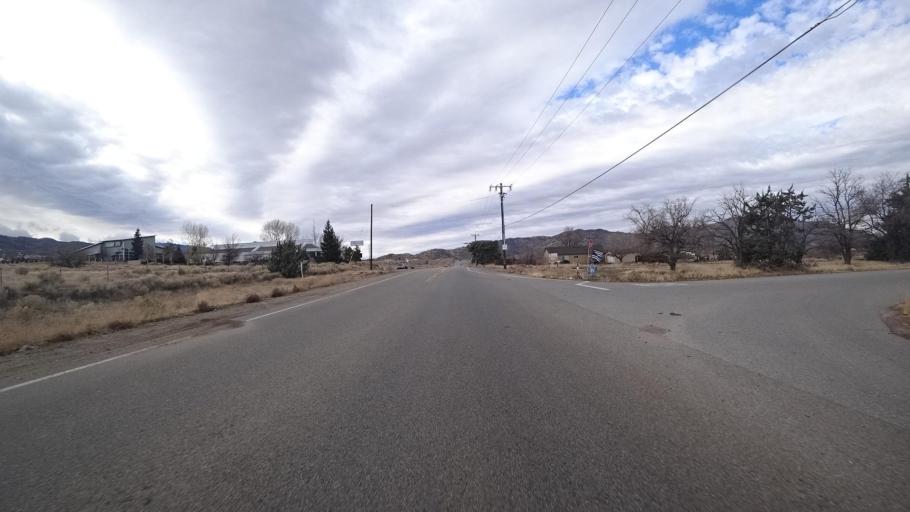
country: US
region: California
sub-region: Kern County
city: Golden Hills
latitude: 35.1242
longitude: -118.4767
